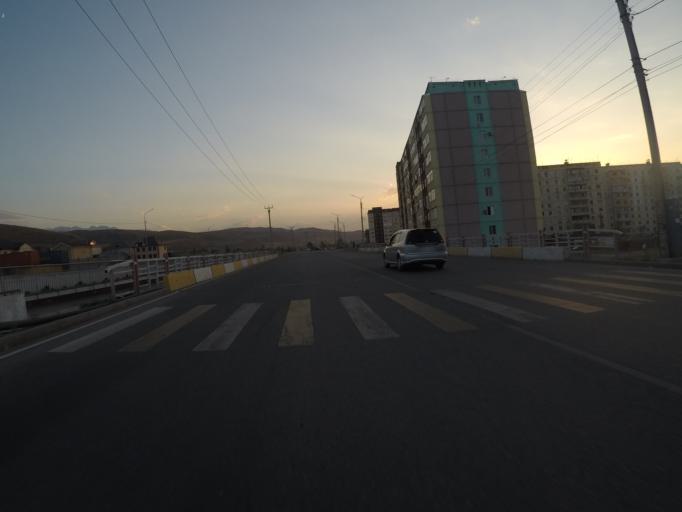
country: KG
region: Chuy
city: Bishkek
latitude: 42.8122
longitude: 74.6428
